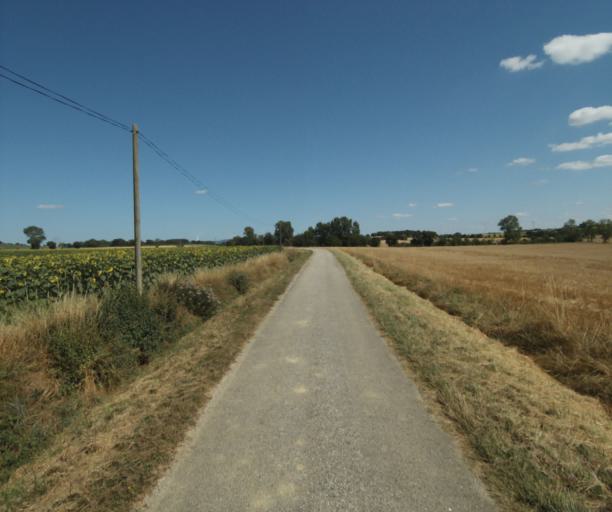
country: FR
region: Midi-Pyrenees
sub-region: Departement de la Haute-Garonne
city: Saint-Felix-Lauragais
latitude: 43.4763
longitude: 1.8916
